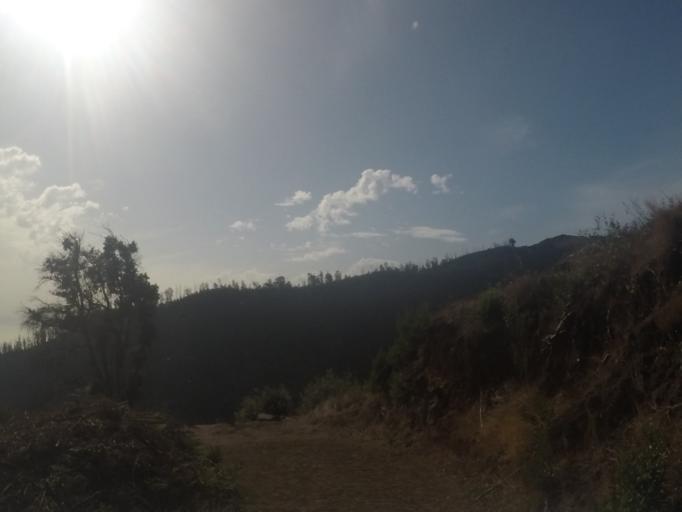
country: PT
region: Madeira
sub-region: Funchal
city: Nossa Senhora do Monte
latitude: 32.6966
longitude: -16.9128
